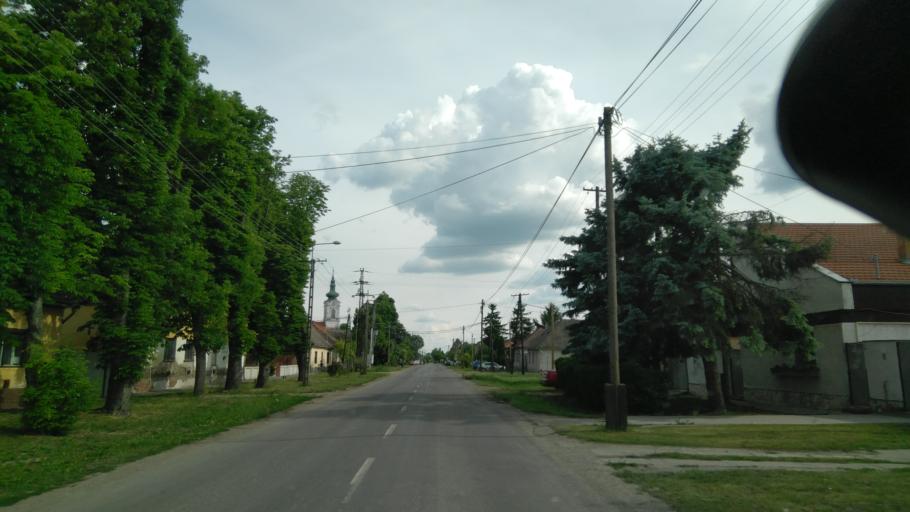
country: HU
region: Bekes
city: Battonya
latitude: 46.2896
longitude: 21.0172
